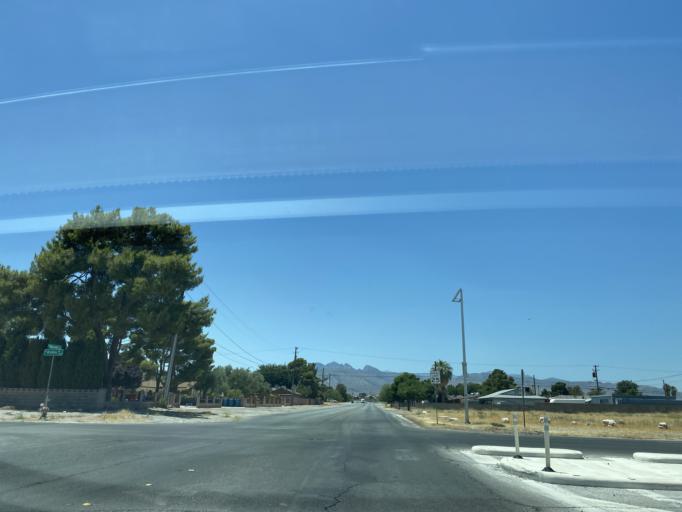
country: US
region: Nevada
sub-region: Clark County
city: Las Vegas
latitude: 36.2319
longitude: -115.2163
